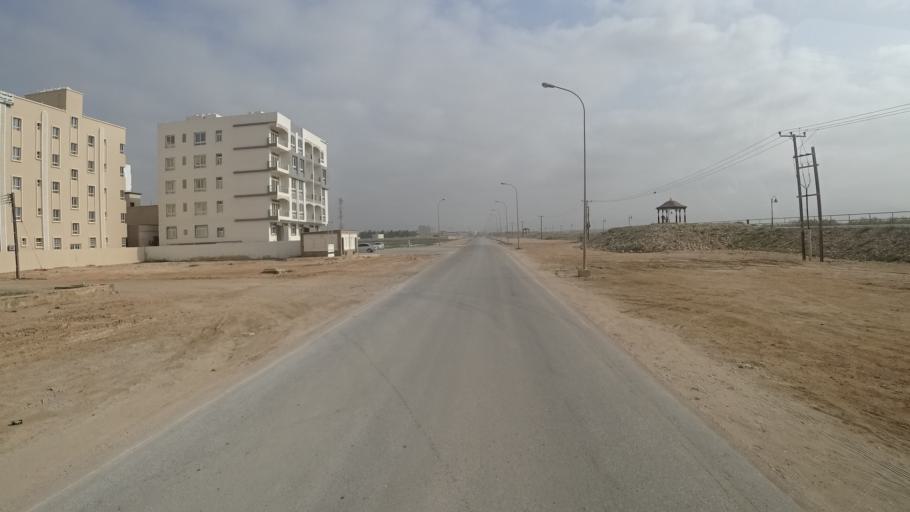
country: OM
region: Zufar
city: Salalah
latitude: 17.0153
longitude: 54.1749
